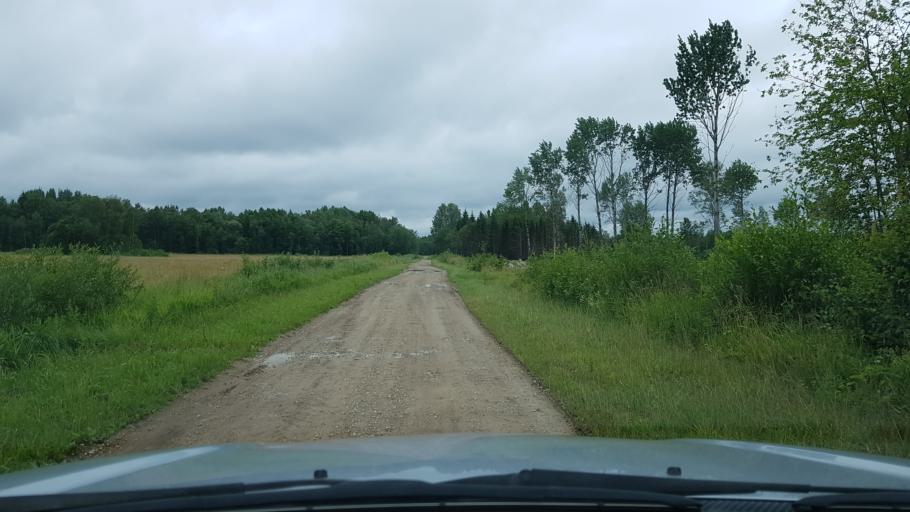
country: EE
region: Ida-Virumaa
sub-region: Narva-Joesuu linn
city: Narva-Joesuu
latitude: 59.3678
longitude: 27.9263
